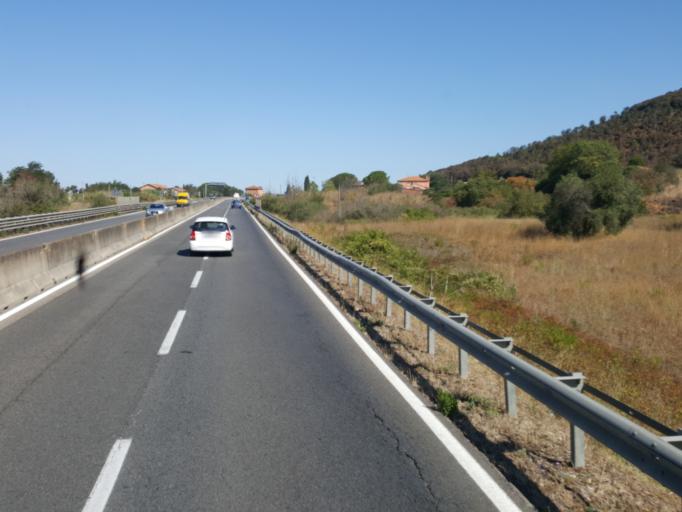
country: IT
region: Tuscany
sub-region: Provincia di Grosseto
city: Fonteblanda
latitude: 42.6337
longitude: 11.1366
